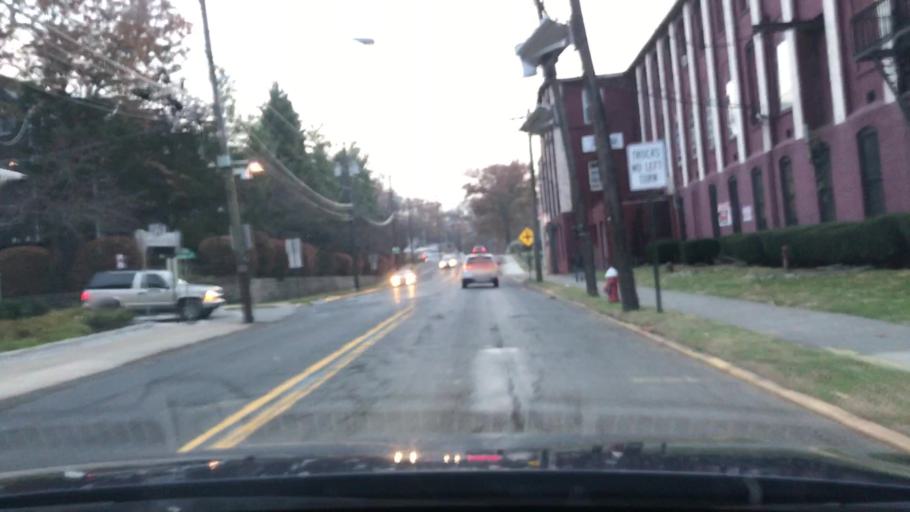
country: US
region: New Jersey
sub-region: Bergen County
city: Wallington
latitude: 40.8434
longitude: -74.1132
